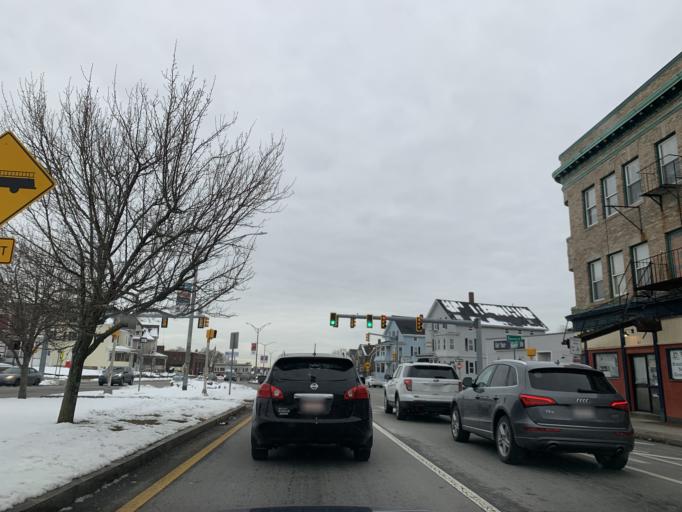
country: US
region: Massachusetts
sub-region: Bristol County
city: Fall River
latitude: 41.6906
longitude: -71.1588
